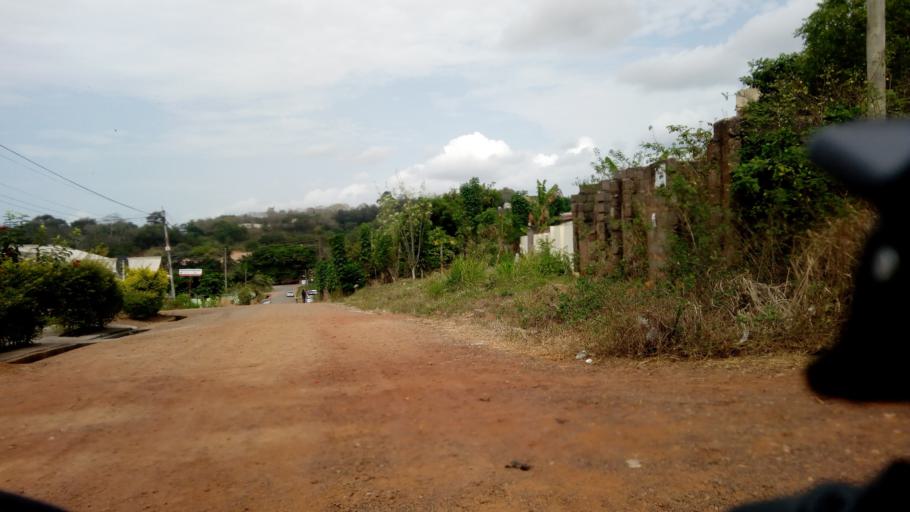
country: GH
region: Central
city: Cape Coast
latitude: 5.1076
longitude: -1.2767
